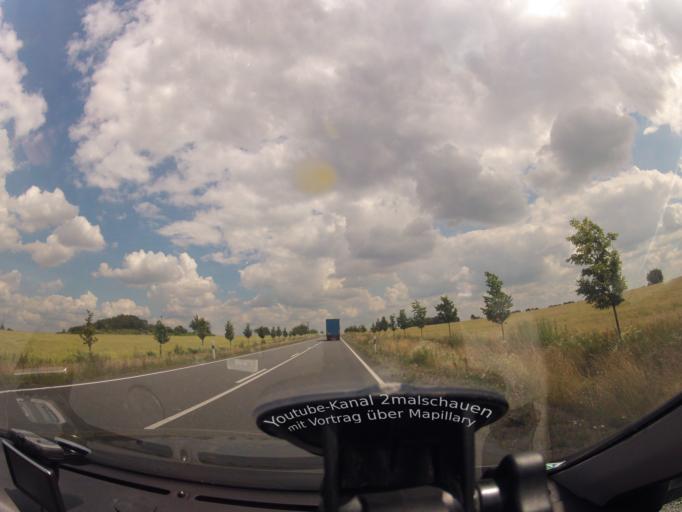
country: DE
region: Saxony
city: Jesewitz
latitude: 51.4334
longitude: 12.5854
